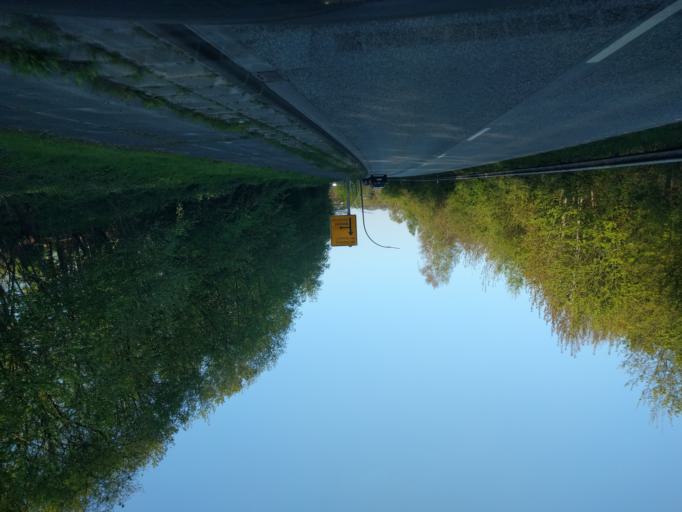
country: DE
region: Lower Saxony
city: Seevetal
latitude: 53.4219
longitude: 9.9663
